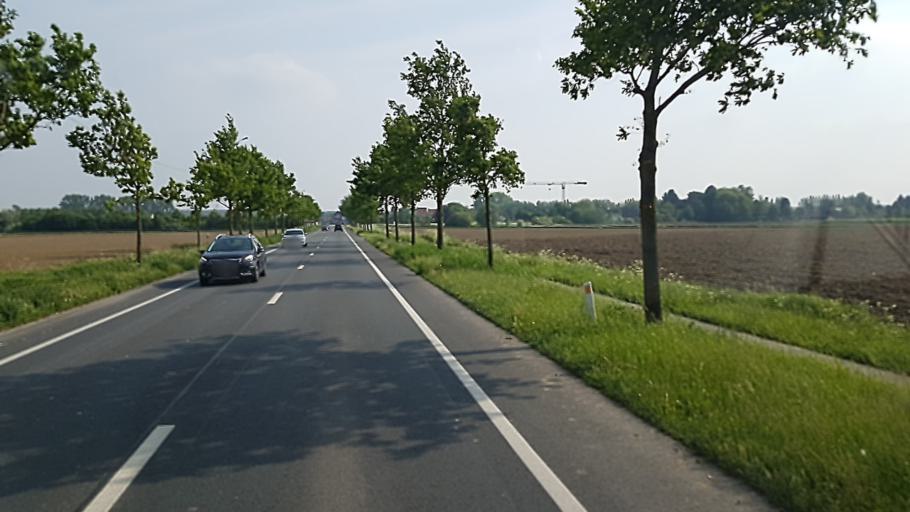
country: BE
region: Wallonia
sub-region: Province du Hainaut
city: Pecq
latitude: 50.7337
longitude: 3.3290
